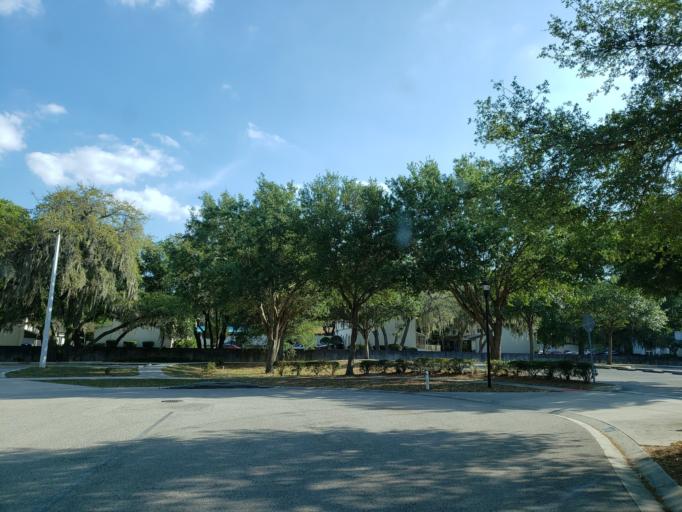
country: US
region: Florida
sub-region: Hillsborough County
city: Brandon
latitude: 27.9292
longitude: -82.2908
